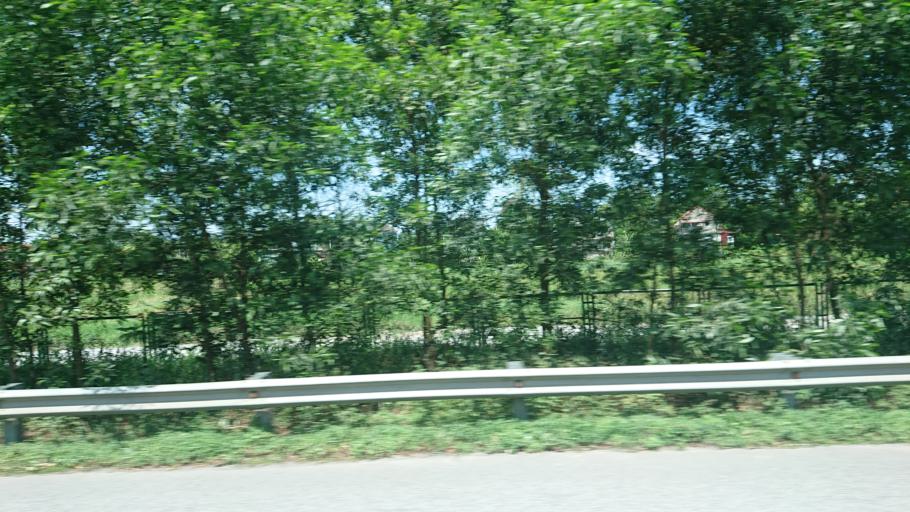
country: VN
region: Ha Nam
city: Thanh Pho Phu Ly
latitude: 20.5781
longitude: 105.9508
